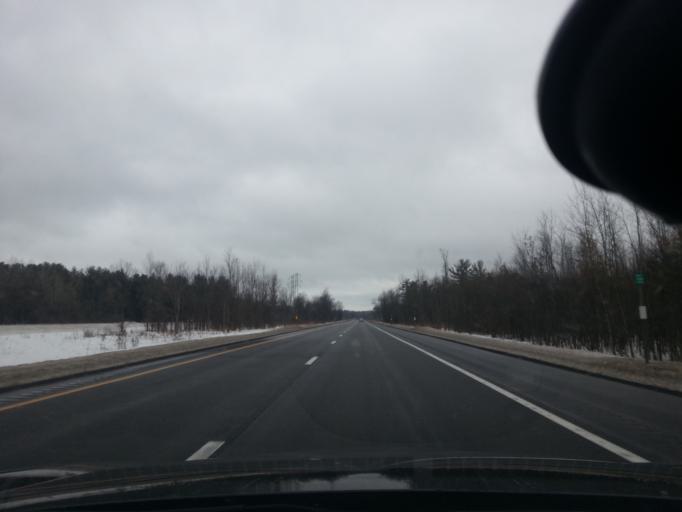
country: US
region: New York
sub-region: Oswego County
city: Central Square
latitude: 43.3435
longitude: -76.1234
